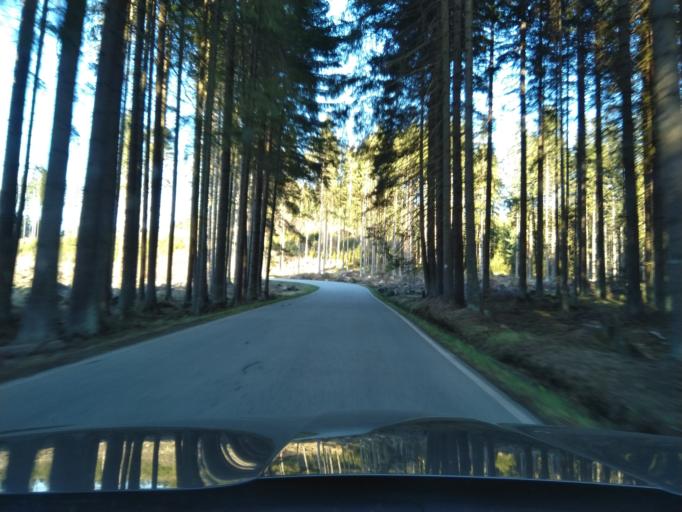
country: CZ
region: Jihocesky
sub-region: Okres Prachatice
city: Volary
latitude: 48.9024
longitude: 13.8183
